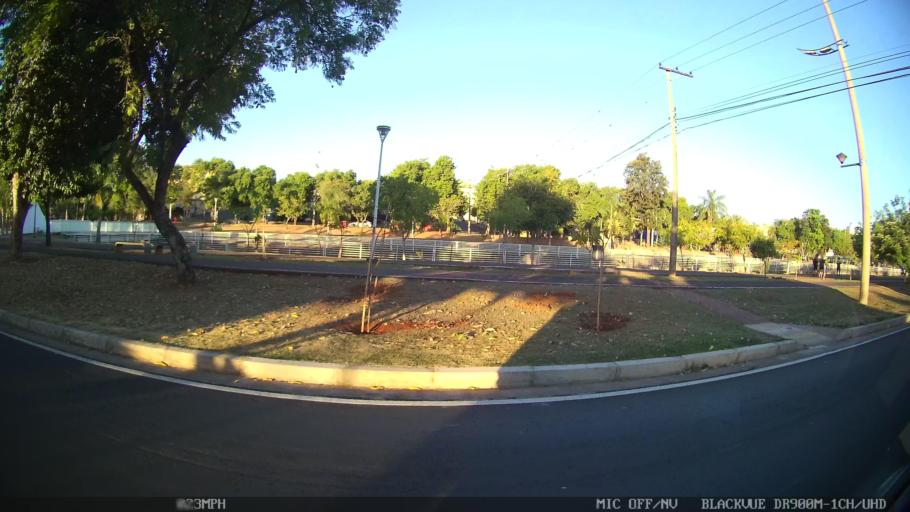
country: BR
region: Sao Paulo
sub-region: Sao Jose Do Rio Preto
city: Sao Jose do Rio Preto
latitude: -20.7908
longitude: -49.3769
